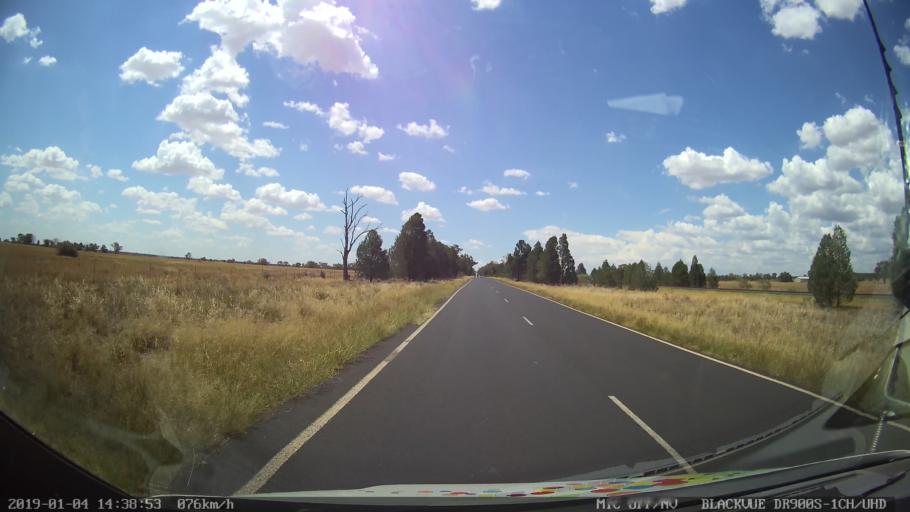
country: AU
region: New South Wales
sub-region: Dubbo Municipality
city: Dubbo
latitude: -32.1713
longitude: 148.6318
